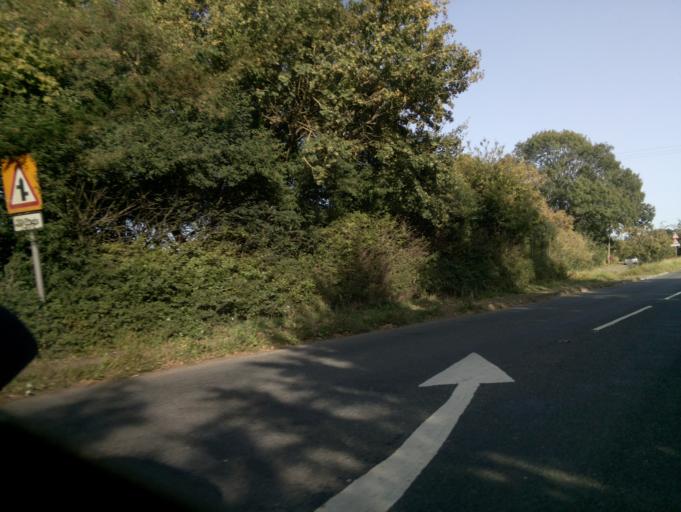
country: GB
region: England
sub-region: Gloucestershire
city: Tewkesbury
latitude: 51.9495
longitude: -2.2288
